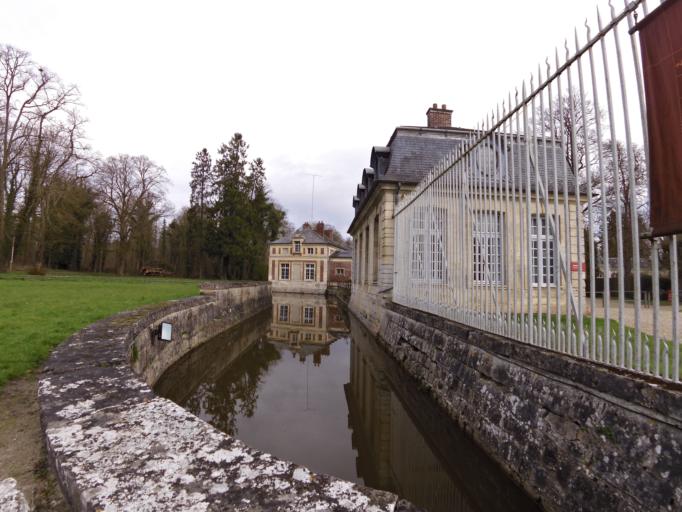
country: FR
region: Picardie
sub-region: Departement de l'Oise
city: Ver-sur-Launette
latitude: 49.1473
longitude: 2.6832
